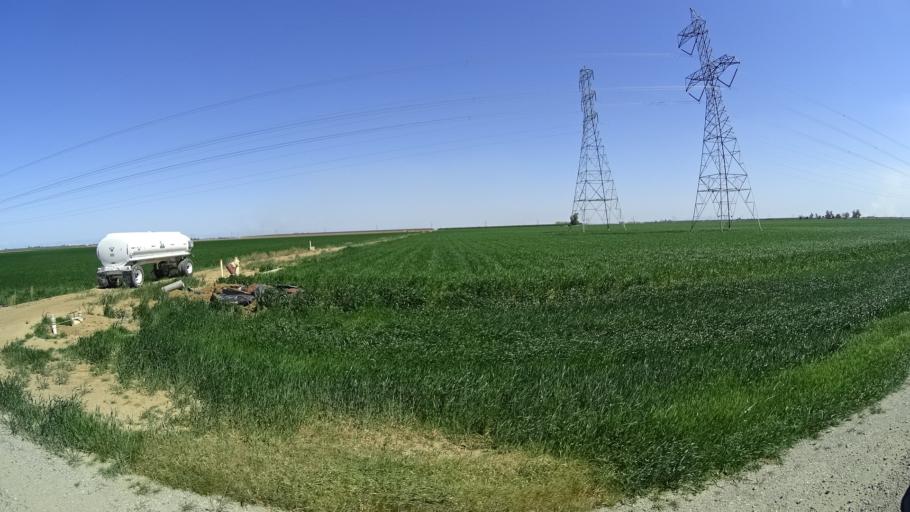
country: US
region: California
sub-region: Glenn County
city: Willows
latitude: 39.4724
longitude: -122.2861
